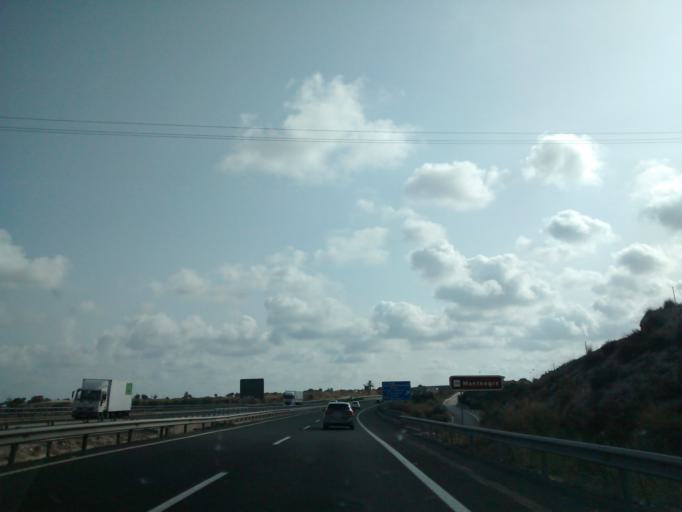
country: ES
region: Valencia
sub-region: Provincia de Alicante
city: el Campello
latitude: 38.4279
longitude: -0.4156
